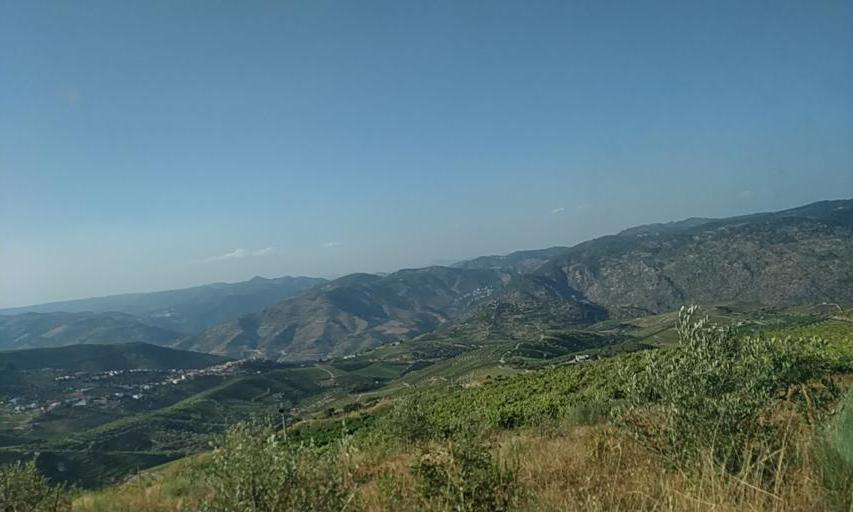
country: PT
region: Viseu
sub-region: Sao Joao da Pesqueira
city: Sao Joao da Pesqueira
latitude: 41.1653
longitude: -7.4102
